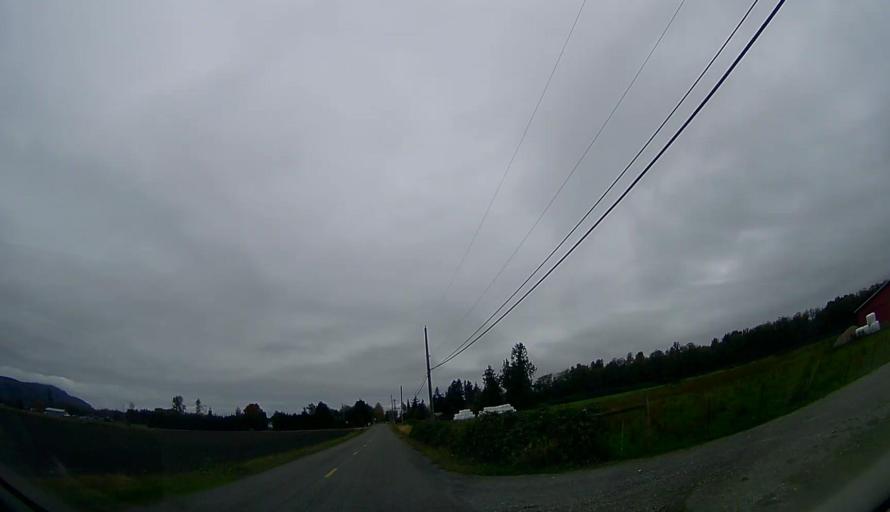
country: US
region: Washington
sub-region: Skagit County
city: Sedro-Woolley
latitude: 48.5146
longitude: -122.1565
